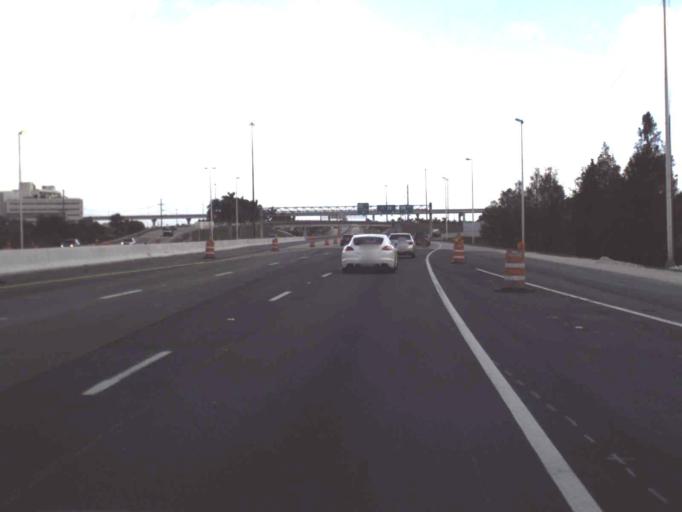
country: US
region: Florida
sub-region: Miami-Dade County
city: Norland
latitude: 25.9346
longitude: -80.2156
